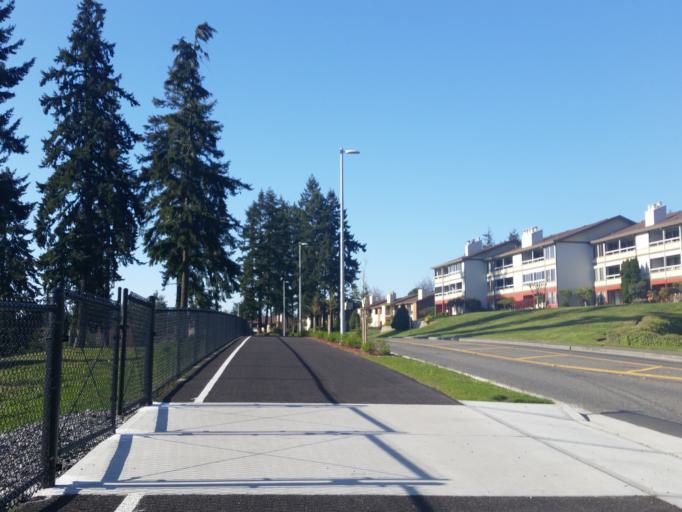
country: US
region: Washington
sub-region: Snohomish County
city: Mountlake Terrace
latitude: 47.7871
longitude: -122.3264
